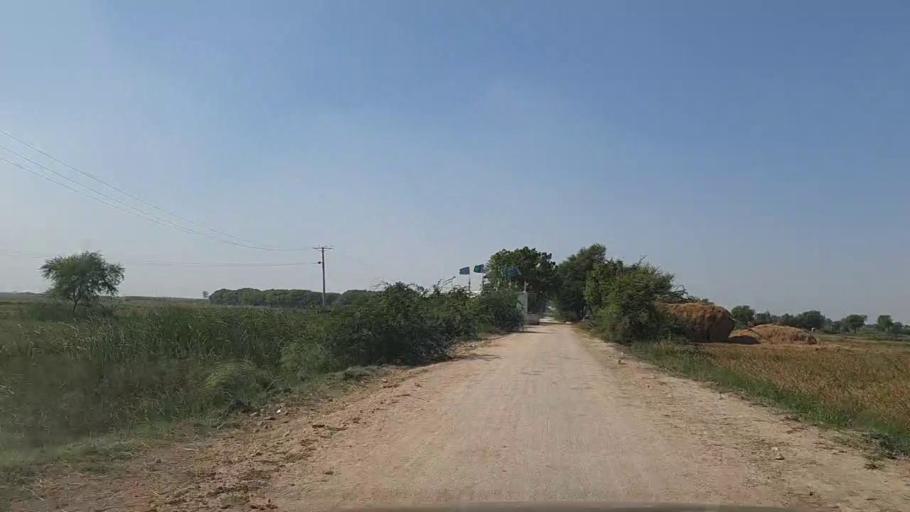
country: PK
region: Sindh
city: Daro Mehar
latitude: 24.8369
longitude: 68.1492
